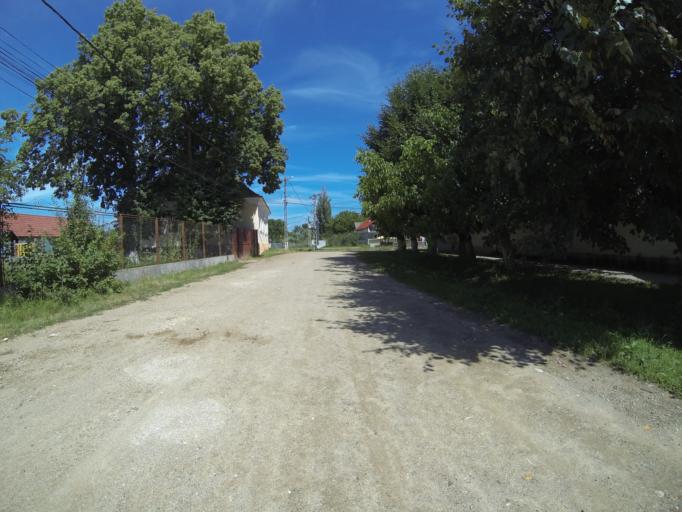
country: RO
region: Brasov
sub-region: Comuna Sinca Veche
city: Sinca Veche
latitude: 45.7648
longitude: 25.1662
